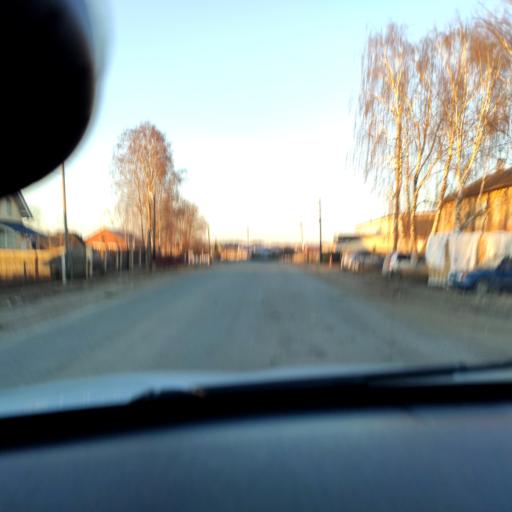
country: RU
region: Perm
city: Kultayevo
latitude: 57.9318
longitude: 55.8774
